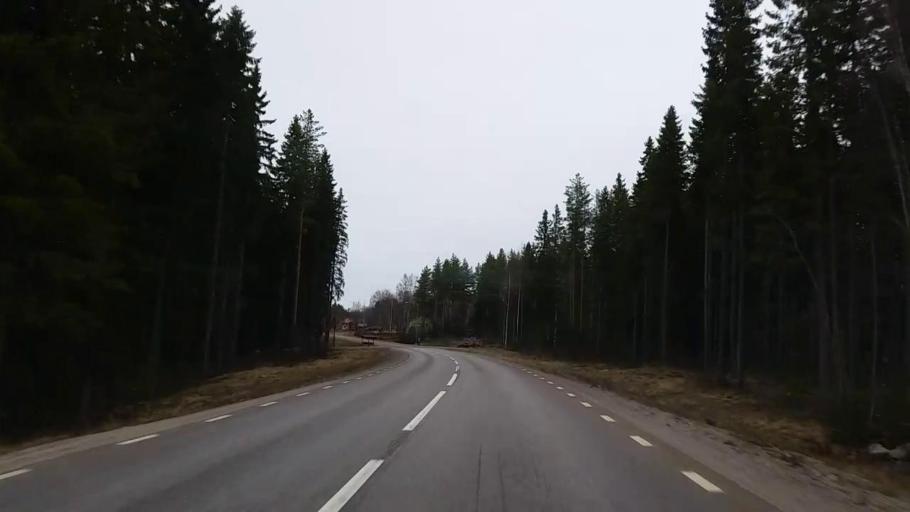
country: SE
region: Gaevleborg
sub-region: Ovanakers Kommun
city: Edsbyn
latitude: 61.2008
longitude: 15.8736
